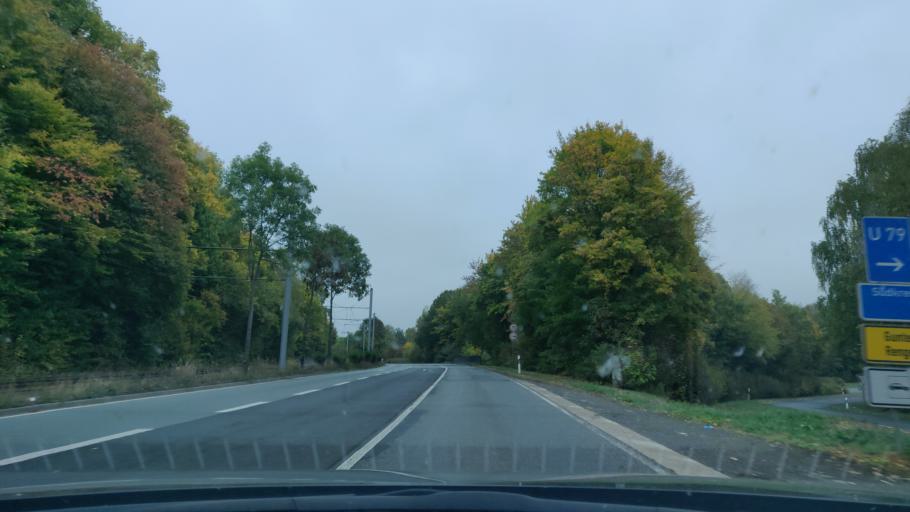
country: DE
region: Hesse
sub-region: Regierungsbezirk Kassel
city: Baunatal
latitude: 51.2649
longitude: 9.4291
